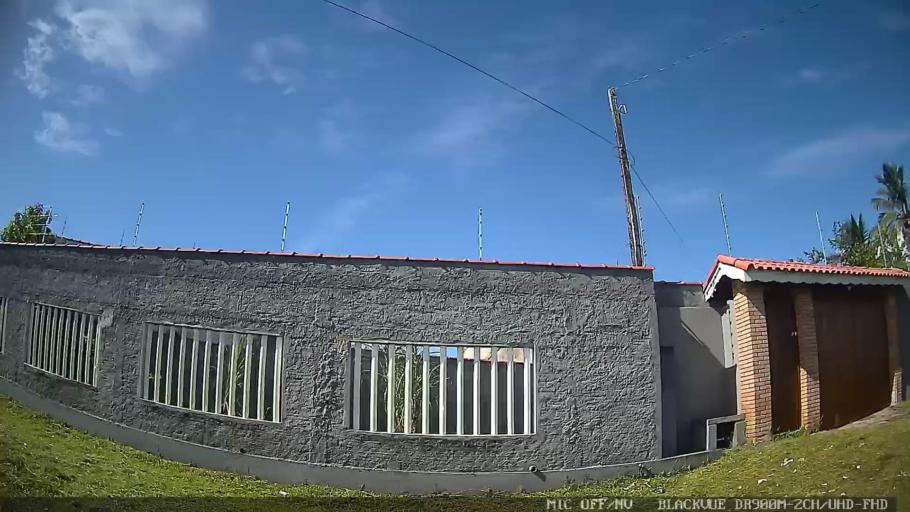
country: BR
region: Sao Paulo
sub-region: Itanhaem
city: Itanhaem
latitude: -24.2363
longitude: -46.8942
